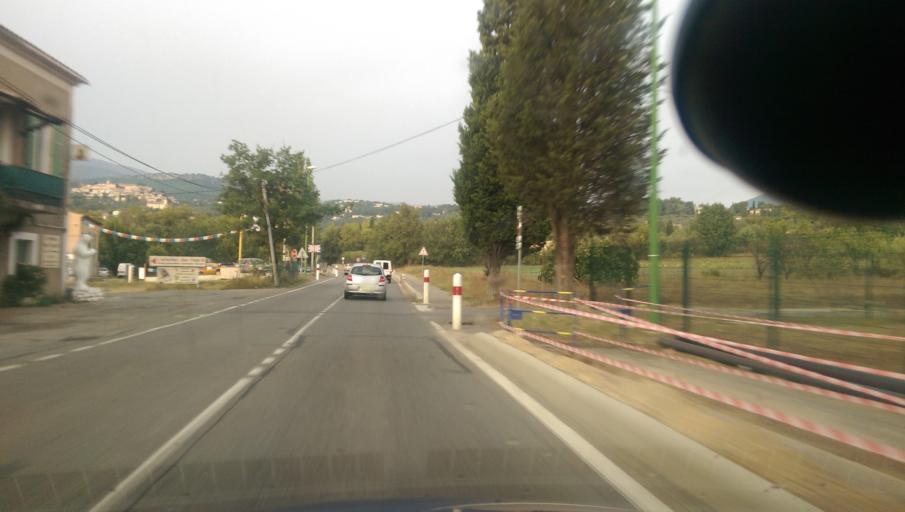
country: FR
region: Provence-Alpes-Cote d'Azur
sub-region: Departement des Alpes-Maritimes
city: Chateauneuf-Grasse
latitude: 43.6618
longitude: 6.9874
